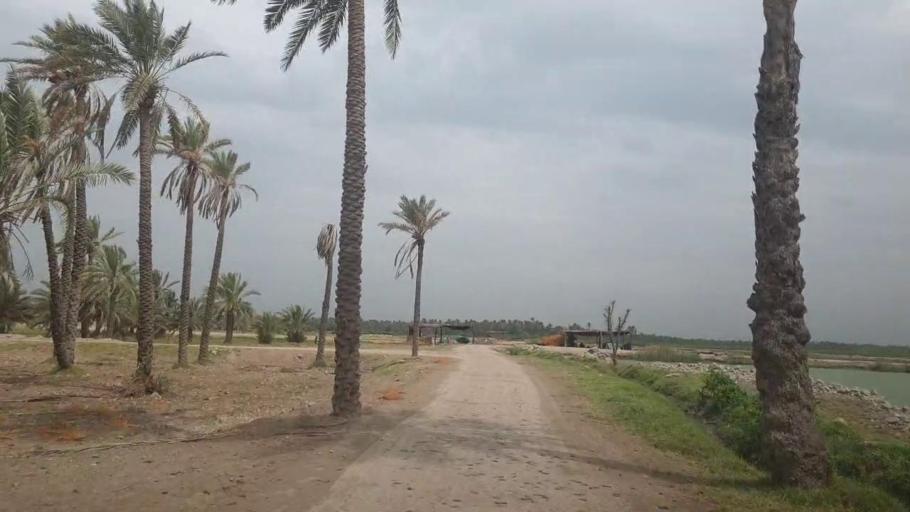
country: PK
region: Sindh
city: Khairpur
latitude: 27.5834
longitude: 68.7401
